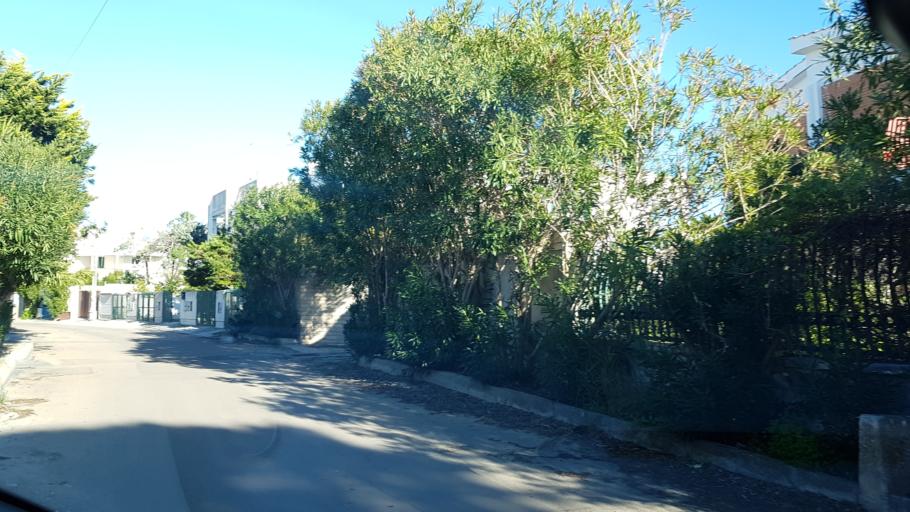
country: IT
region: Apulia
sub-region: Provincia di Lecce
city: Gallipoli
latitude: 40.0355
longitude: 18.0184
